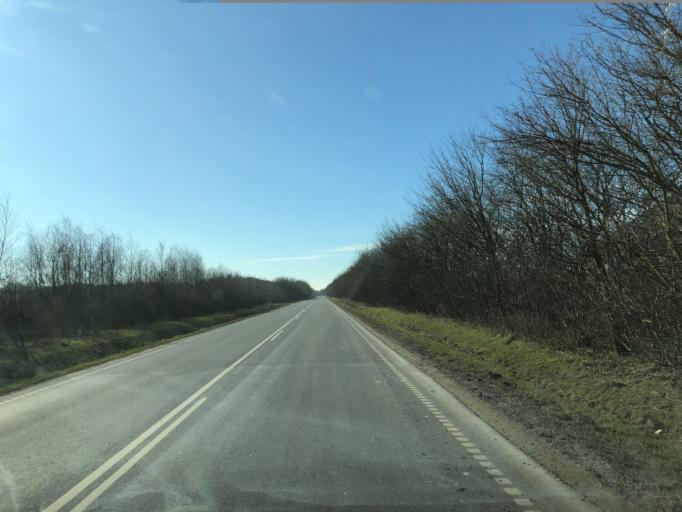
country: DK
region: Central Jutland
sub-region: Ikast-Brande Kommune
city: Bording Kirkeby
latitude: 56.1495
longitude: 9.2254
